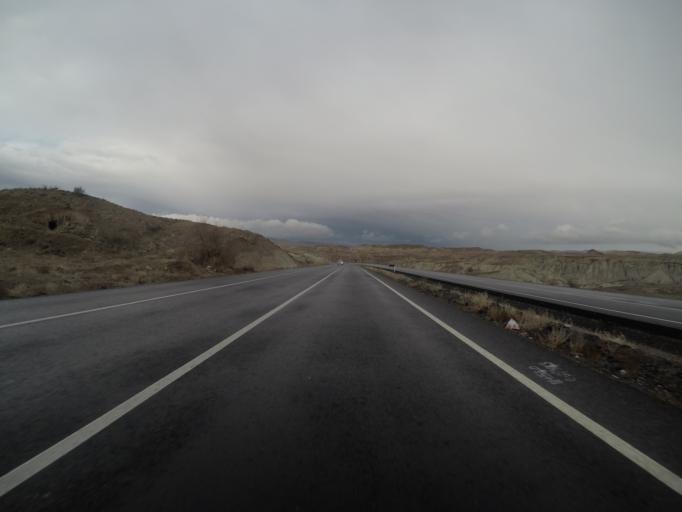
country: TR
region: Nevsehir
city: Avanos
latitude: 38.6901
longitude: 34.8143
